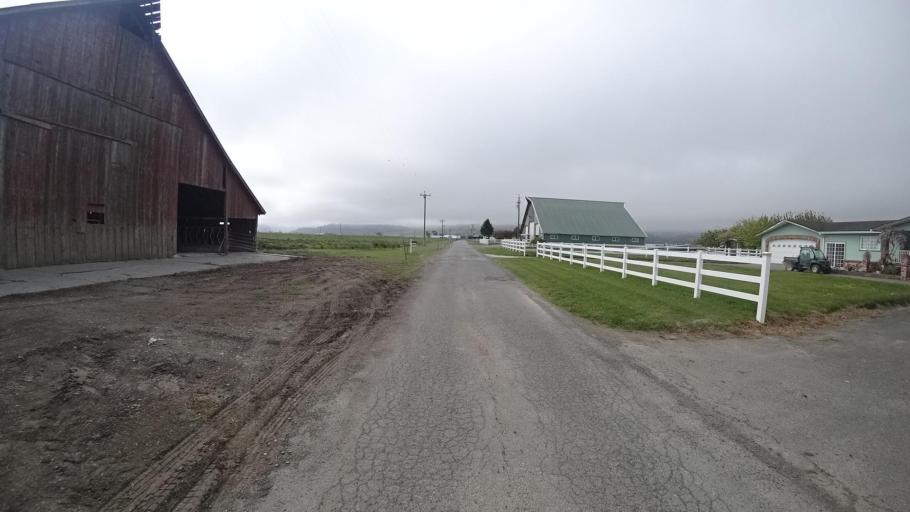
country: US
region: California
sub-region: Humboldt County
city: Fortuna
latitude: 40.5797
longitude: -124.1878
